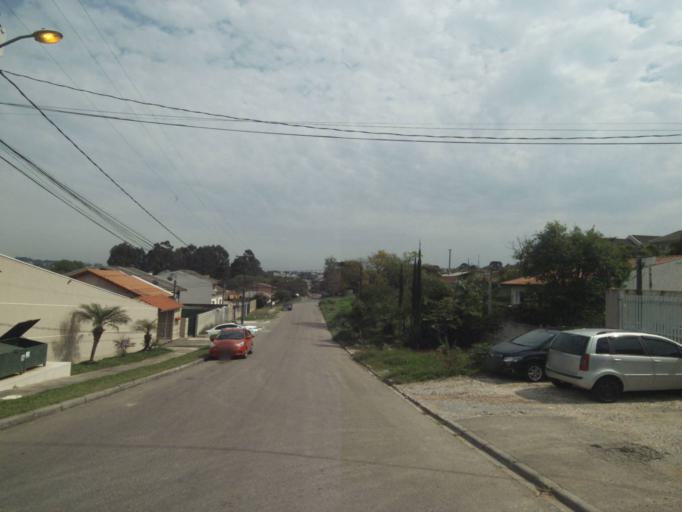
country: BR
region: Parana
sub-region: Pinhais
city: Pinhais
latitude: -25.4252
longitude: -49.2081
